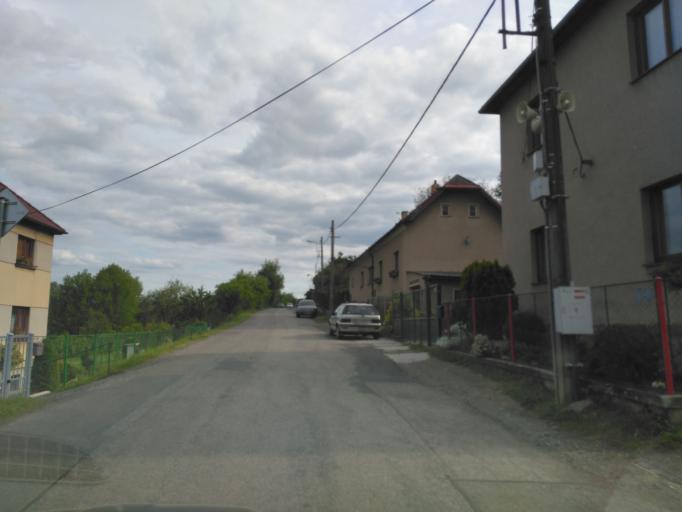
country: CZ
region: Central Bohemia
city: Zdice
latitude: 49.8985
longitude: 13.9607
